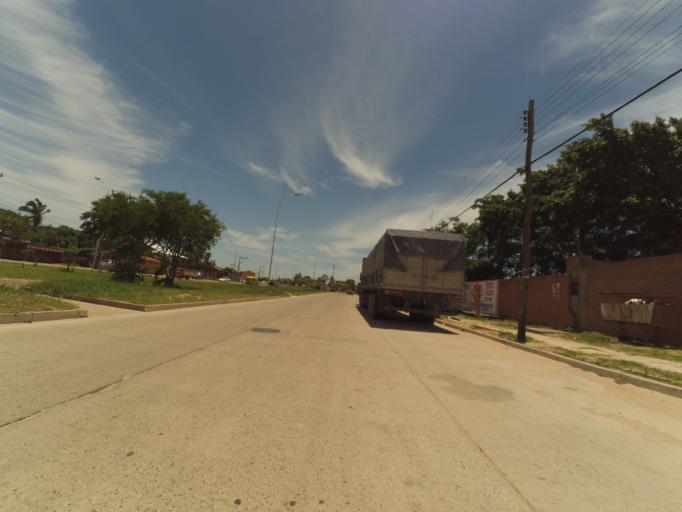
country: BO
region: Santa Cruz
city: Santa Cruz de la Sierra
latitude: -17.8109
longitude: -63.2208
